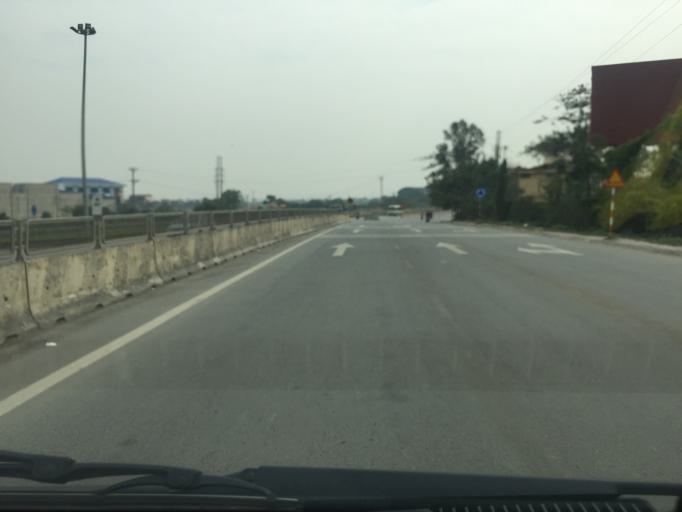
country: VN
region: Ninh Binh
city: Thanh Pho Ninh Binh
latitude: 20.2278
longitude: 105.9675
